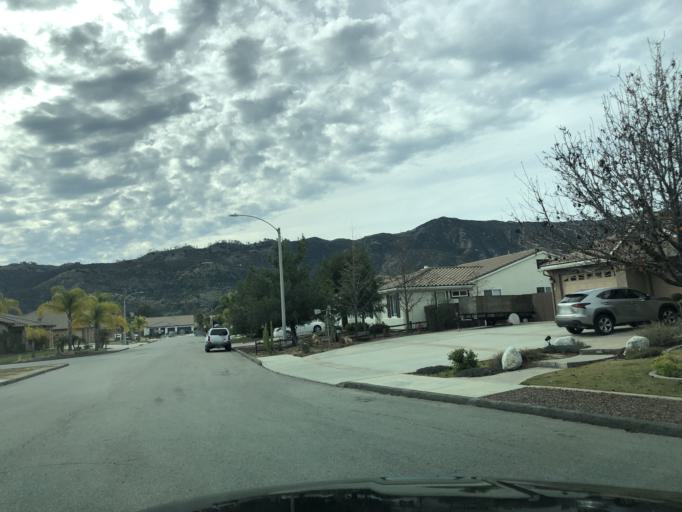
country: US
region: California
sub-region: Riverside County
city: Wildomar
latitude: 33.6108
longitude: -117.2879
